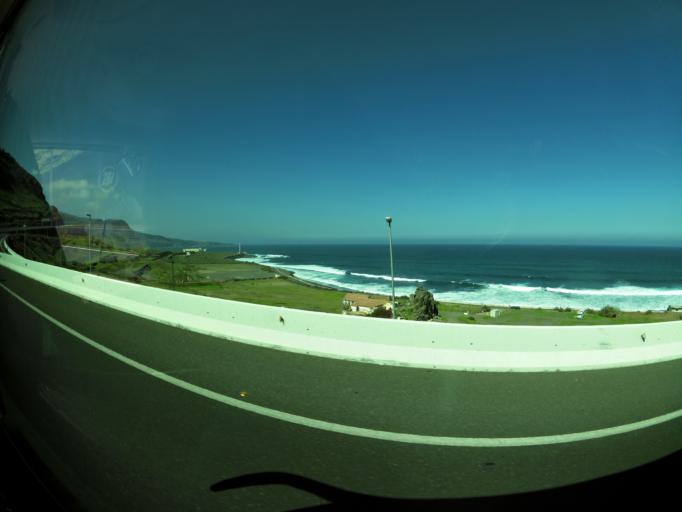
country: ES
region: Canary Islands
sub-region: Provincia de Las Palmas
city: Firgas
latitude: 28.1426
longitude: -15.5787
